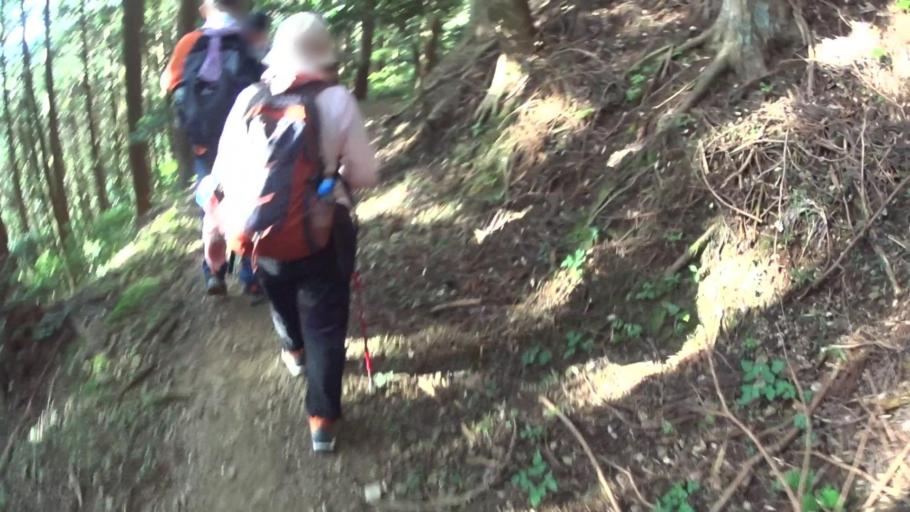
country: JP
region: Shiga Prefecture
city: Kitahama
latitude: 35.1072
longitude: 135.8430
